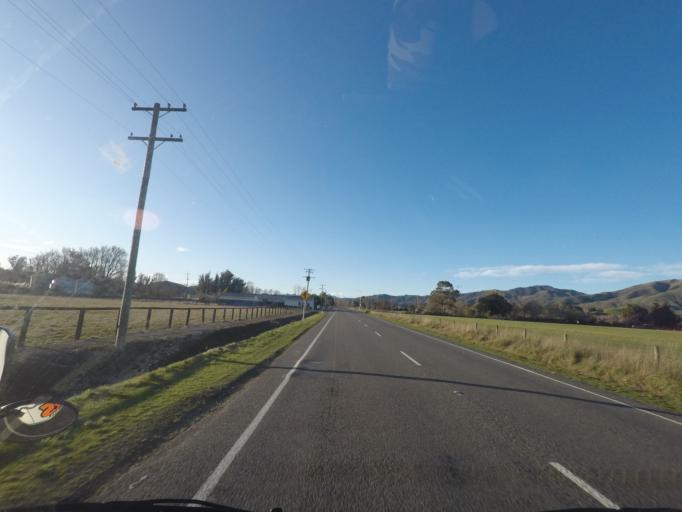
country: NZ
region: Canterbury
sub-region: Kaikoura District
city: Kaikoura
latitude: -42.7145
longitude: 173.2898
